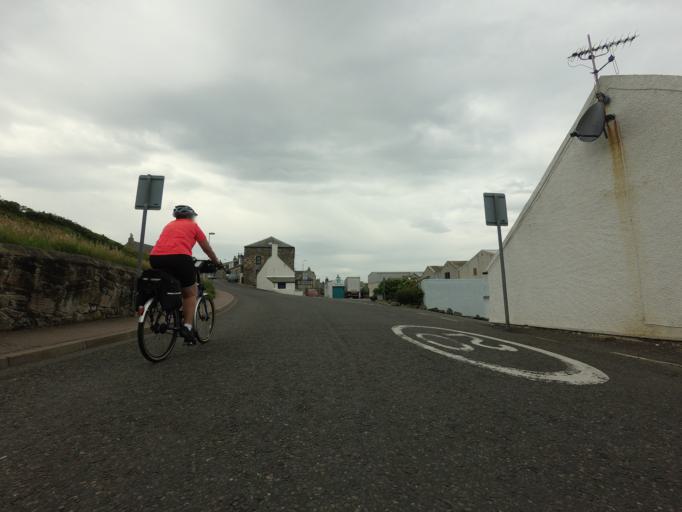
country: GB
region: Scotland
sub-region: Aberdeenshire
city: Whitehills
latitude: 57.6790
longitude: -2.5794
